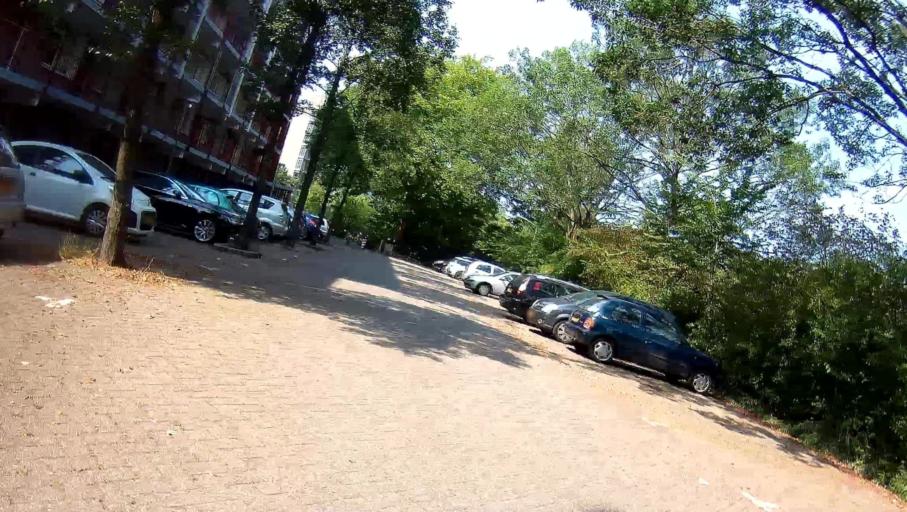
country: NL
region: South Holland
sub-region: Gemeente Leidschendam-Voorburg
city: Voorburg
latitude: 52.0796
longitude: 4.3722
